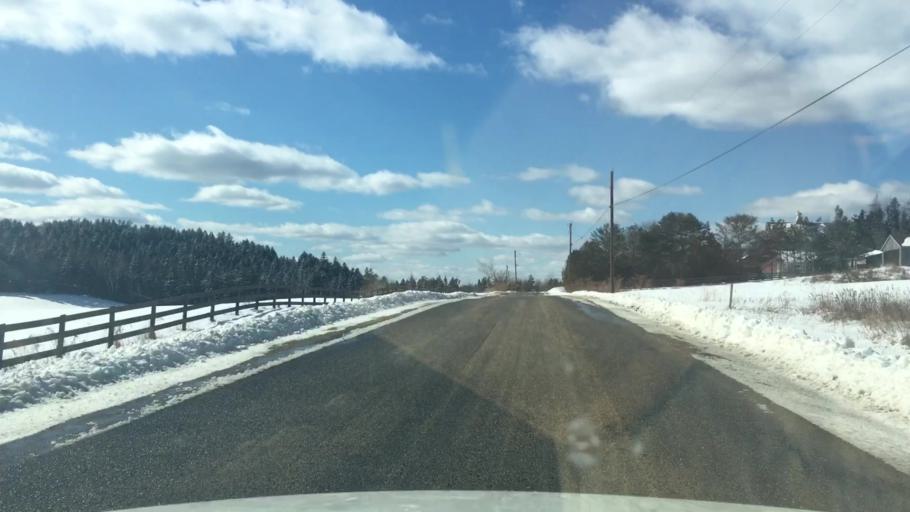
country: US
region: Maine
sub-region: Washington County
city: Machiasport
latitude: 44.6699
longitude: -67.4357
